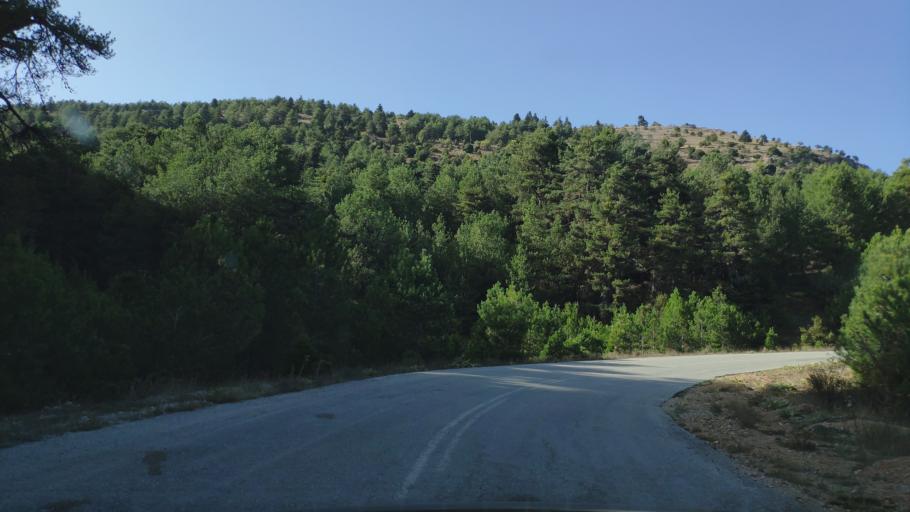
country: GR
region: West Greece
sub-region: Nomos Achaias
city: Aiyira
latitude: 38.0259
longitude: 22.4019
